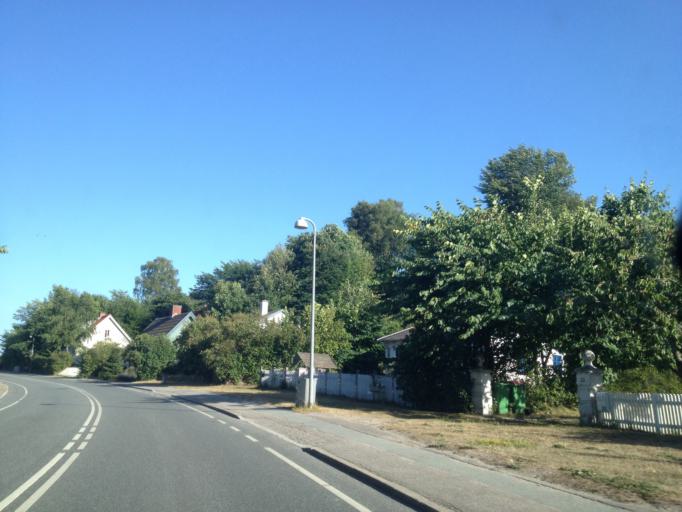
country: DK
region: Capital Region
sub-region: Gribskov Kommune
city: Helsinge
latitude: 56.0523
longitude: 12.1060
